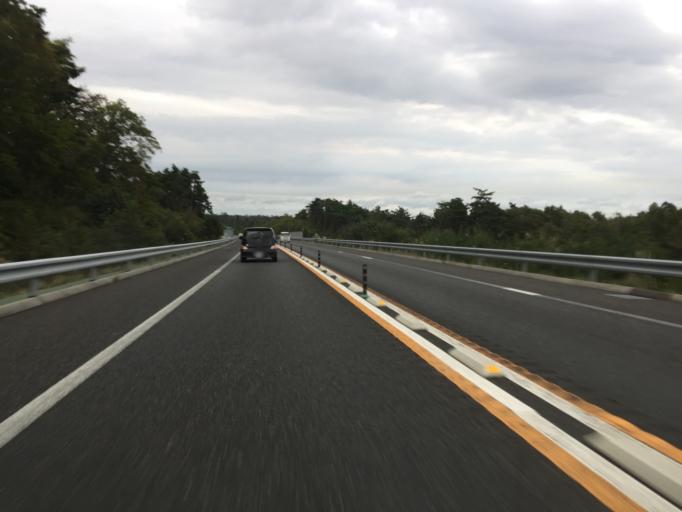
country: JP
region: Fukushima
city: Namie
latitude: 37.6982
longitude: 140.9225
